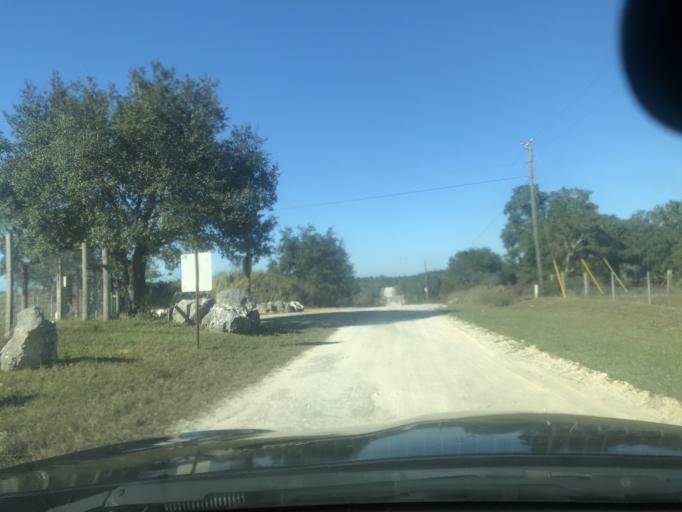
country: US
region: Florida
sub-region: Citrus County
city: Lecanto
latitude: 28.8201
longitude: -82.5180
